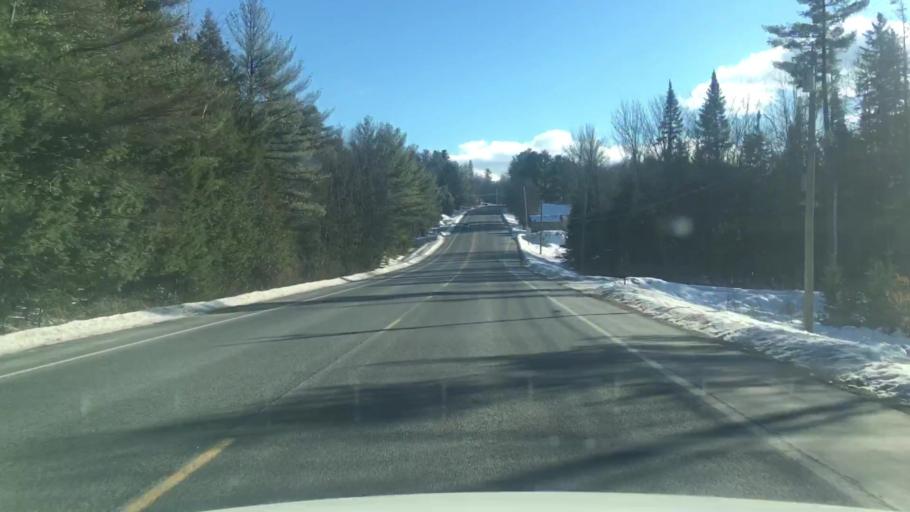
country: US
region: Maine
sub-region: Somerset County
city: Madison
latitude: 44.9028
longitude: -69.8132
